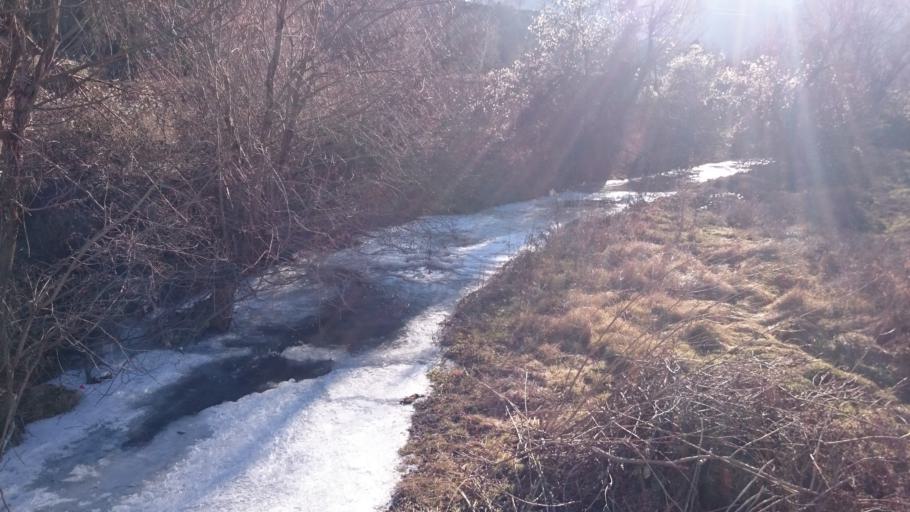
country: MK
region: Makedonski Brod
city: Makedonski Brod
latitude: 41.5104
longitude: 21.2263
